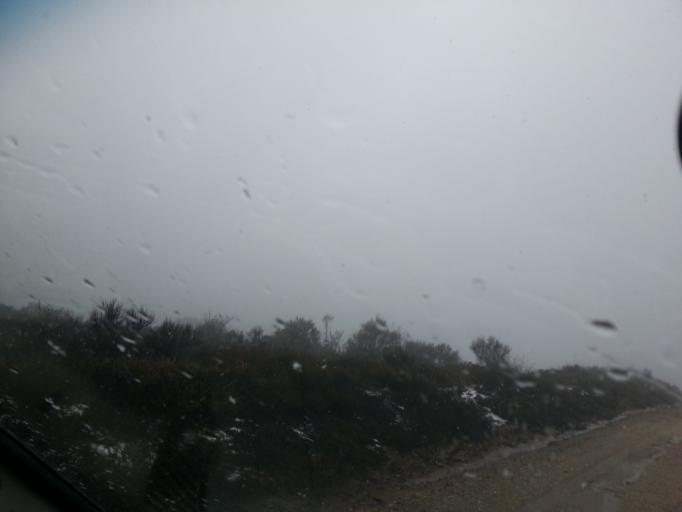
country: PT
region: Guarda
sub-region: Celorico da Beira
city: Celorico da Beira
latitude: 40.5315
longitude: -7.4458
